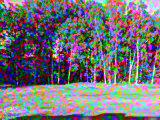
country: SE
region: Soedermanland
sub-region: Flens Kommun
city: Flen
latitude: 59.0638
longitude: 16.5936
